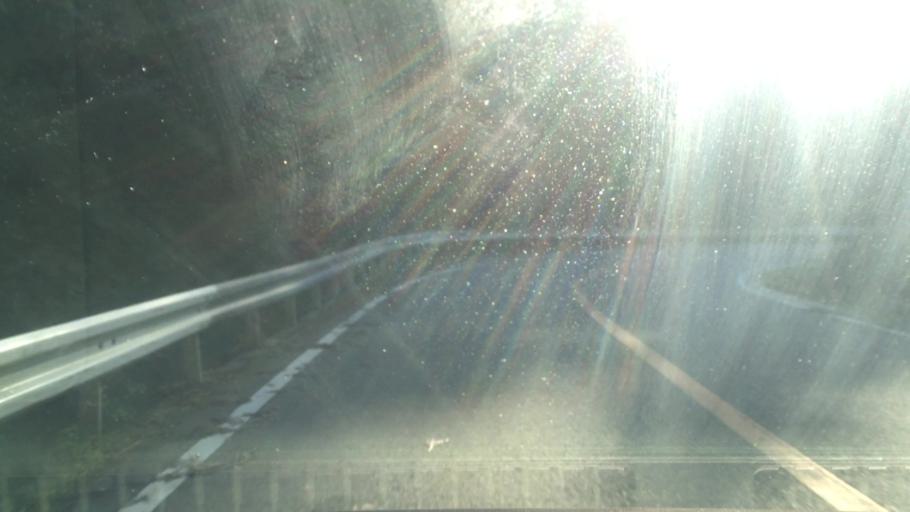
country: JP
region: Hyogo
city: Toyooka
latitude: 35.6162
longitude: 134.8533
